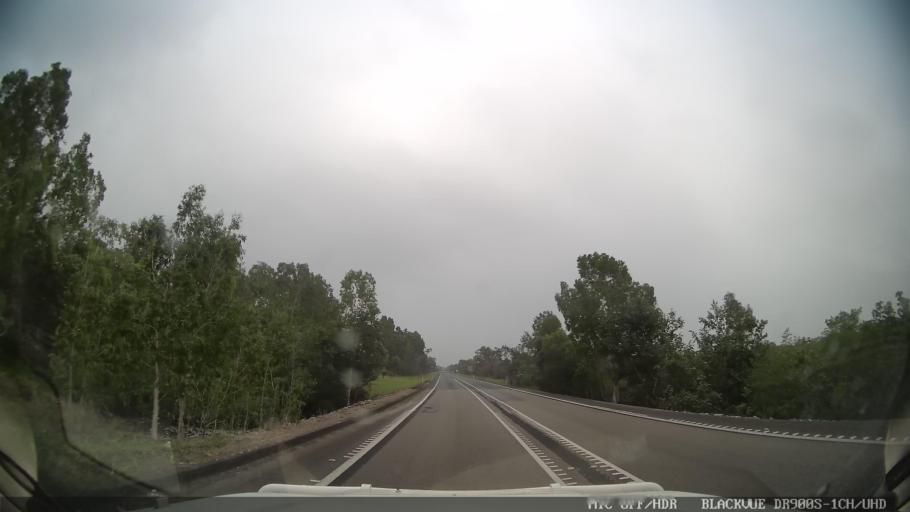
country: AU
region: Queensland
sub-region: Hinchinbrook
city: Ingham
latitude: -18.5061
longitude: 146.1872
